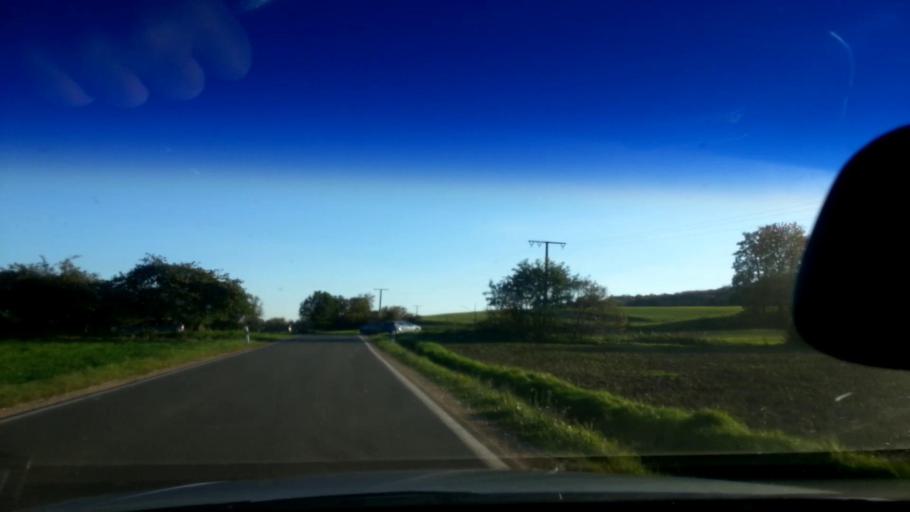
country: DE
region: Bavaria
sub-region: Upper Franconia
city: Rattelsdorf
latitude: 50.0129
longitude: 10.8726
